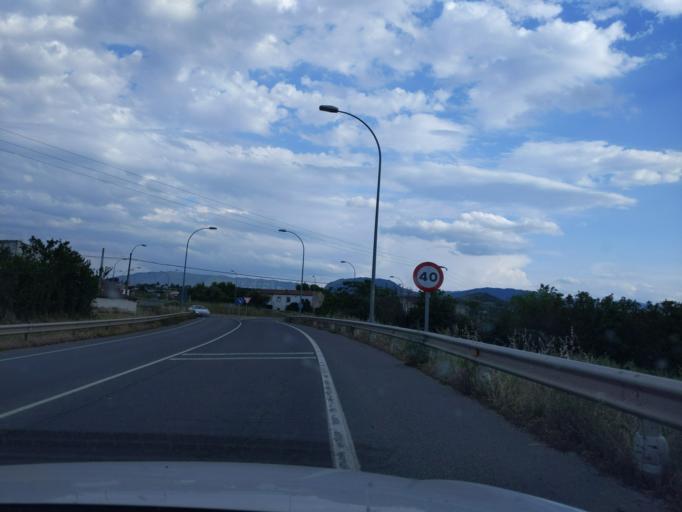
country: ES
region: La Rioja
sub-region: Provincia de La Rioja
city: Villamediana de Iregua
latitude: 42.4242
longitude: -2.4248
